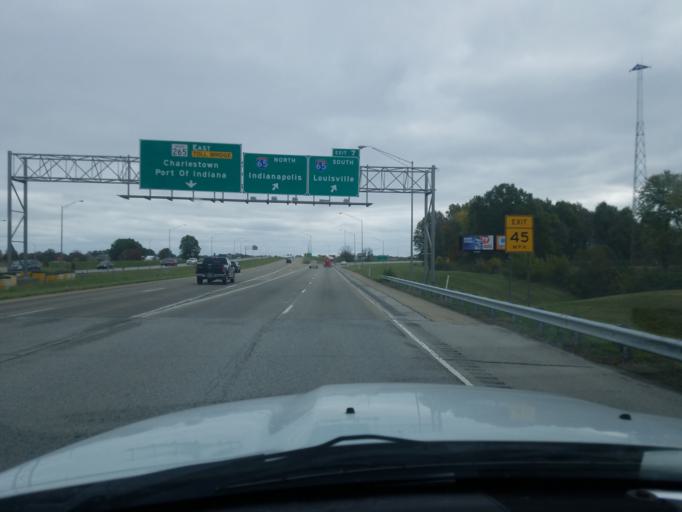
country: US
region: Indiana
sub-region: Clark County
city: Clarksville
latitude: 38.3454
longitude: -85.7609
